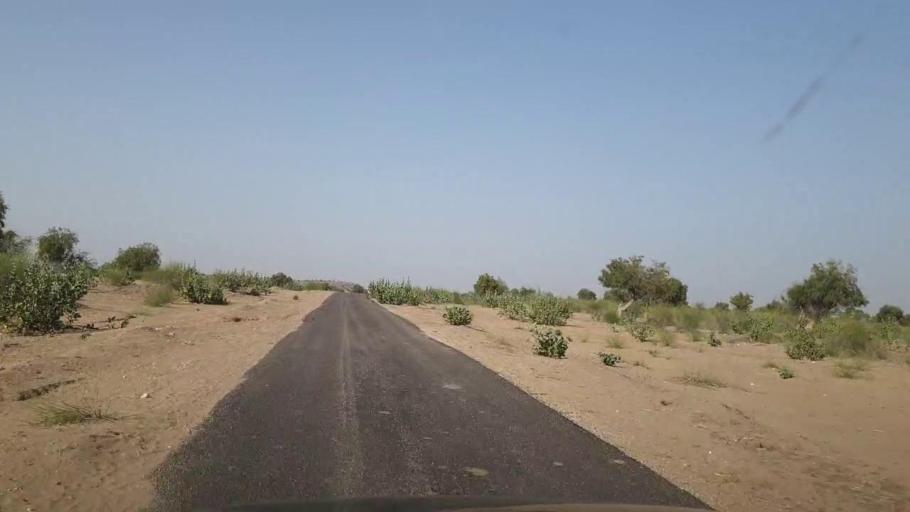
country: PK
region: Sindh
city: Islamkot
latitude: 25.1548
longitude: 70.5217
